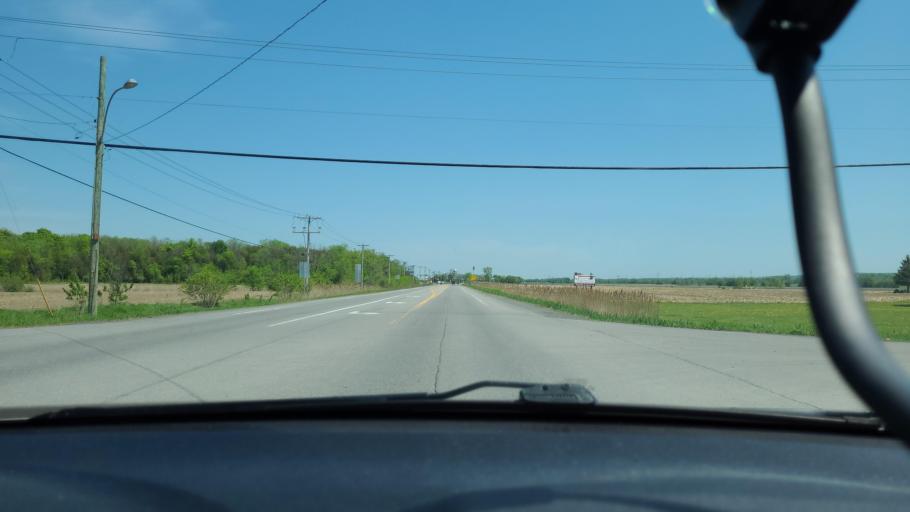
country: CA
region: Quebec
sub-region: Laurentides
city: Mirabel
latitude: 45.6190
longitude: -74.0998
